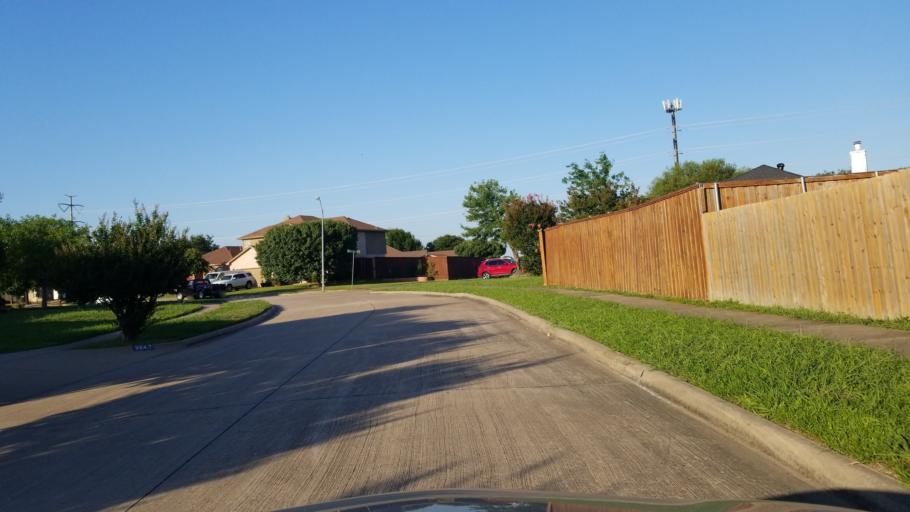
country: US
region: Texas
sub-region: Dallas County
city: Grand Prairie
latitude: 32.6932
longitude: -97.0364
